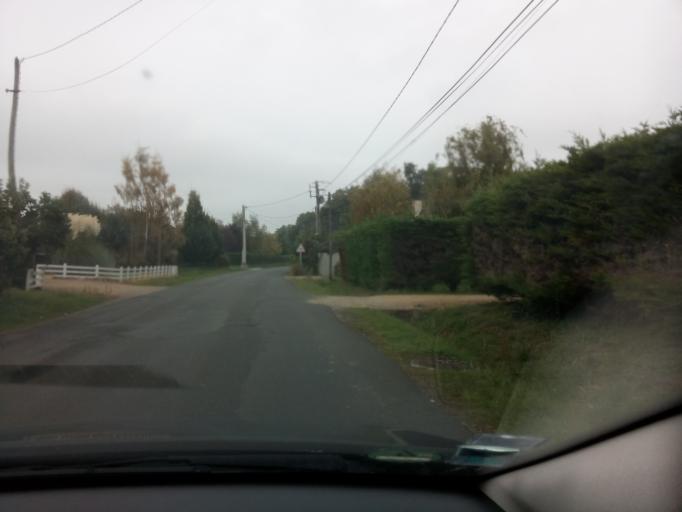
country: FR
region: Pays de la Loire
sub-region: Departement de Maine-et-Loire
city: Soulaire-et-Bourg
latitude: 47.6170
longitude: -0.5567
